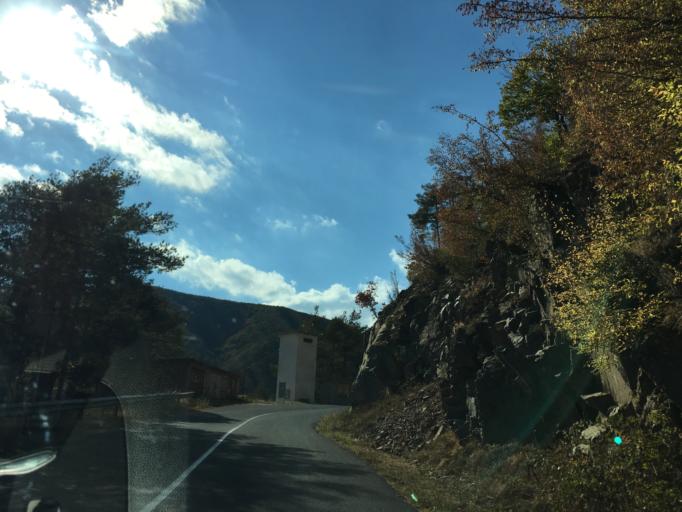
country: BG
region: Smolyan
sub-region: Obshtina Nedelino
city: Nedelino
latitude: 41.4385
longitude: 25.0115
